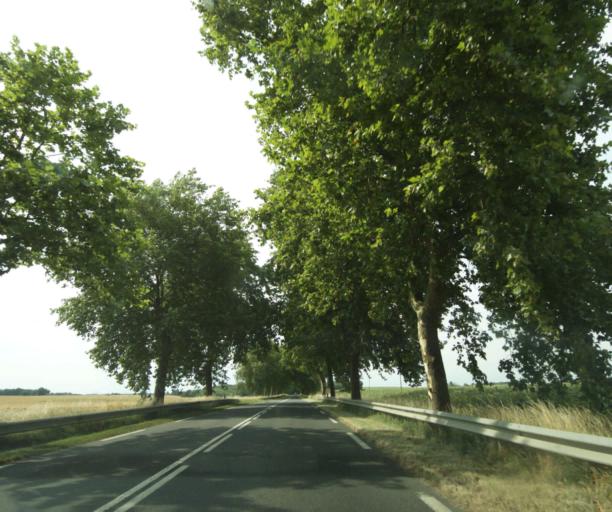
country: FR
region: Centre
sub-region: Departement d'Indre-et-Loire
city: Saint-Paterne-Racan
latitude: 47.6068
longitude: 0.5134
